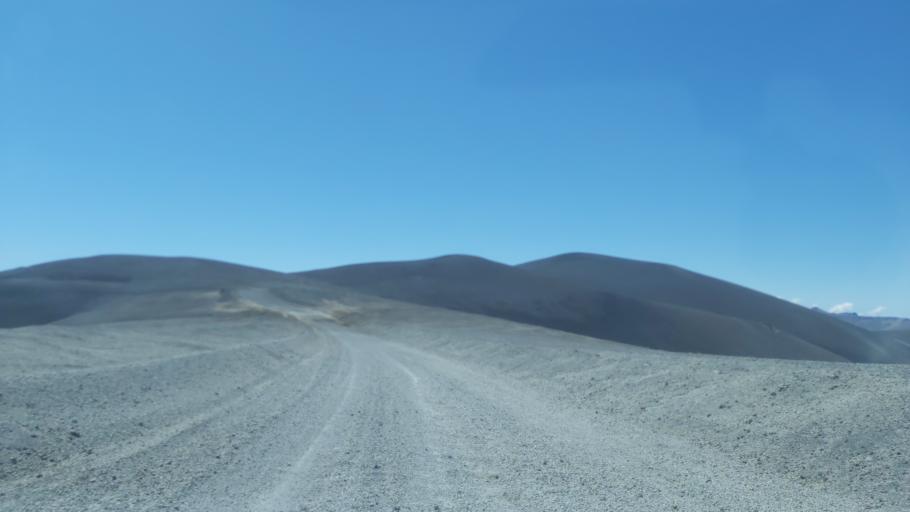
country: CL
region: Araucania
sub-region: Provincia de Cautin
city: Vilcun
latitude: -38.3764
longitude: -71.5408
